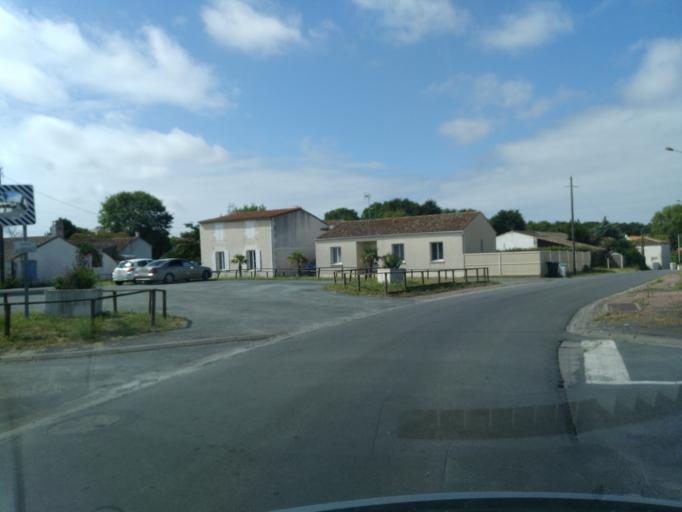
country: FR
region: Poitou-Charentes
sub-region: Departement de la Charente-Maritime
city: Breuillet
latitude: 45.6894
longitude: -1.0711
